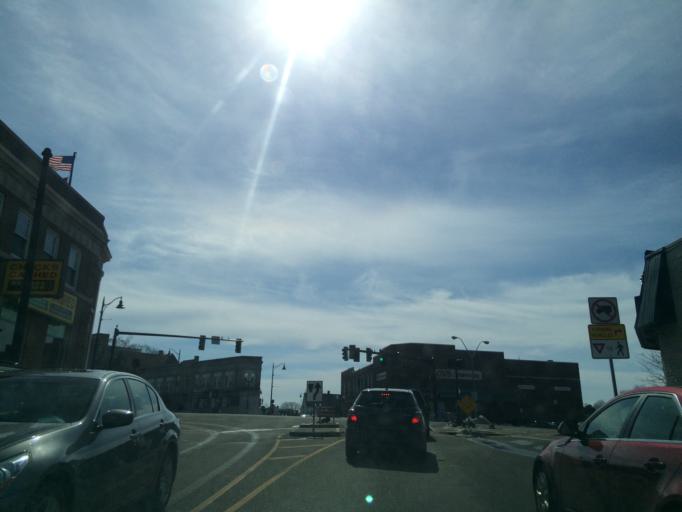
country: US
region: Massachusetts
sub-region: Middlesex County
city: Somerville
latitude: 42.3978
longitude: -71.1045
